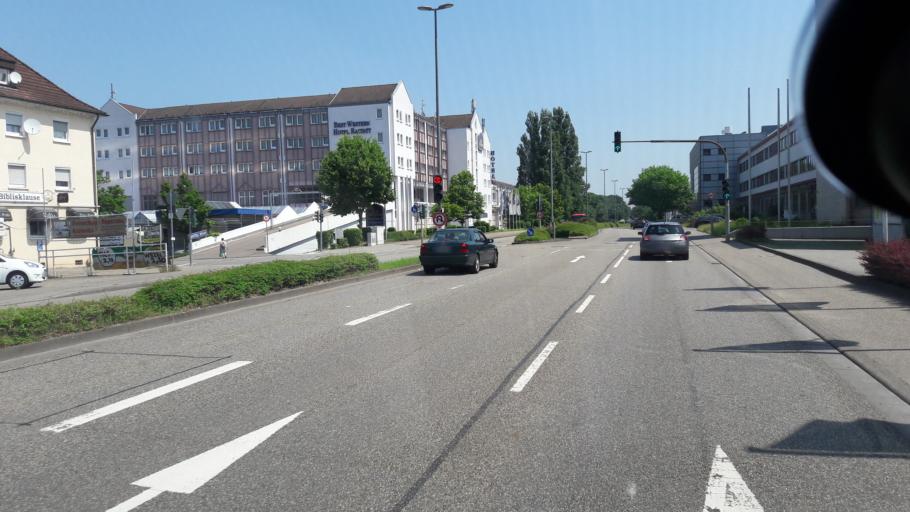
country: DE
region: Baden-Wuerttemberg
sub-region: Karlsruhe Region
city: Rastatt
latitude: 48.8641
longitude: 8.2180
